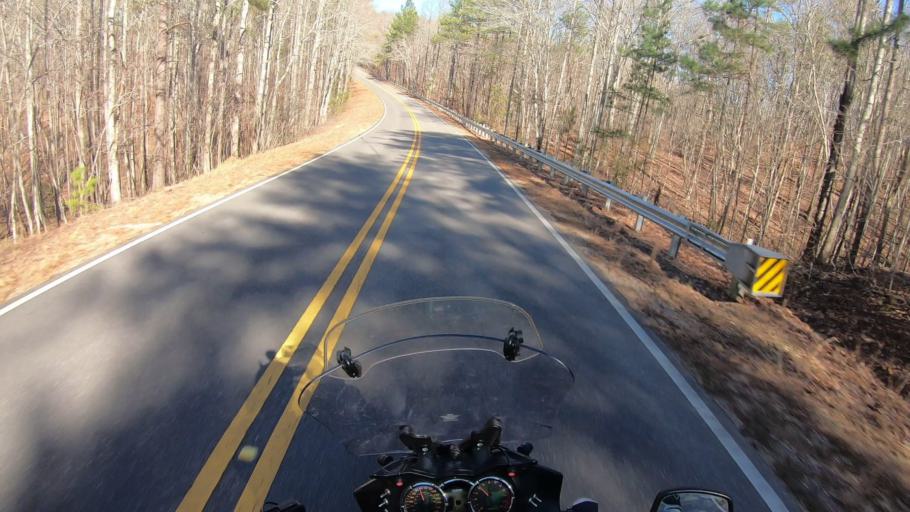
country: US
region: Alabama
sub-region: Calhoun County
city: Choccolocco
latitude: 33.5379
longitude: -85.7337
